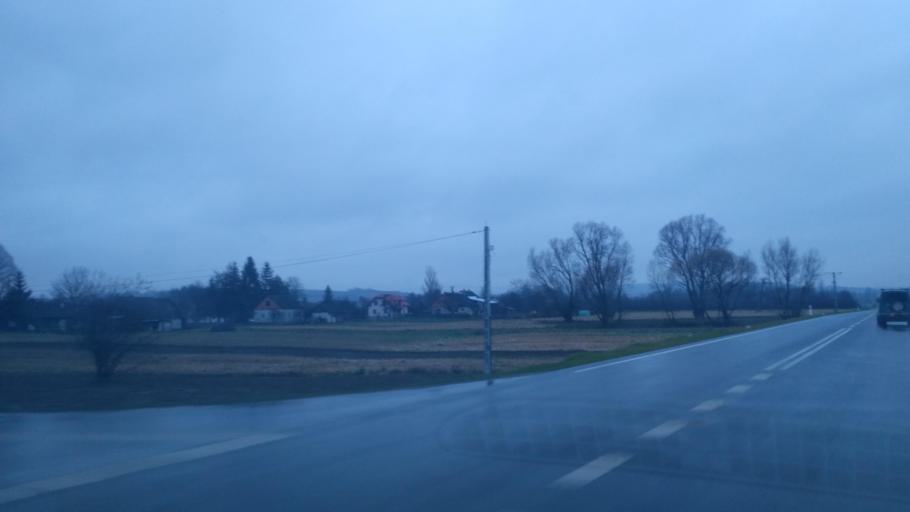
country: PL
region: Subcarpathian Voivodeship
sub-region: Powiat rzeszowski
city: Dynow
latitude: 49.8232
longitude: 22.2412
